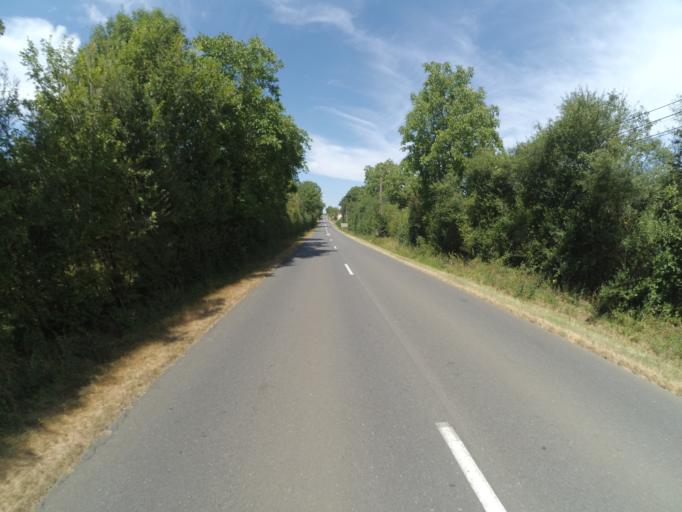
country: FR
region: Poitou-Charentes
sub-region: Departement de la Vienne
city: Usson-du-Poitou
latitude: 46.2674
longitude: 0.5204
